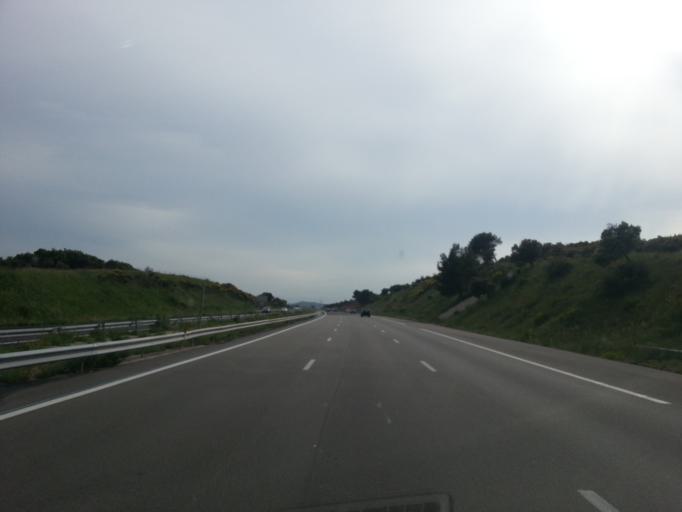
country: FR
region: Languedoc-Roussillon
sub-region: Departement du Gard
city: Tavel
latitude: 43.9972
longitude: 4.6943
